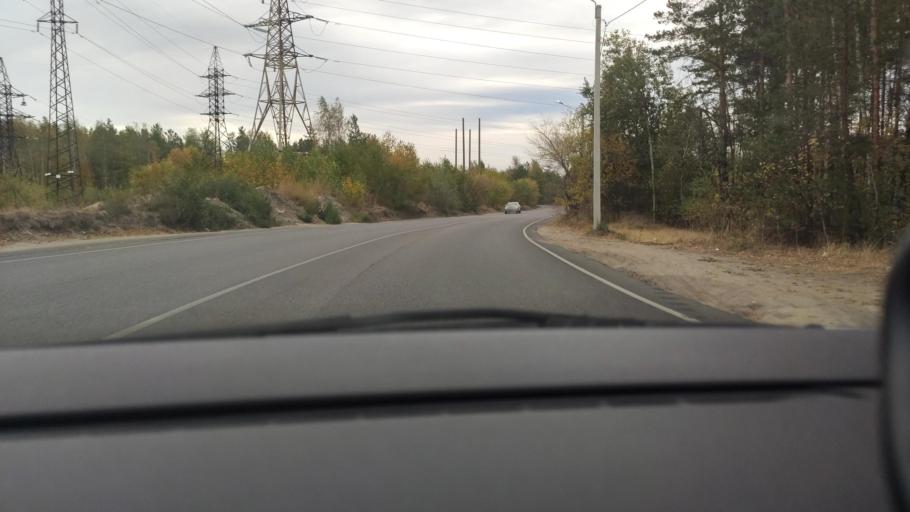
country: RU
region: Voronezj
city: Pridonskoy
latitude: 51.6787
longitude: 39.1122
